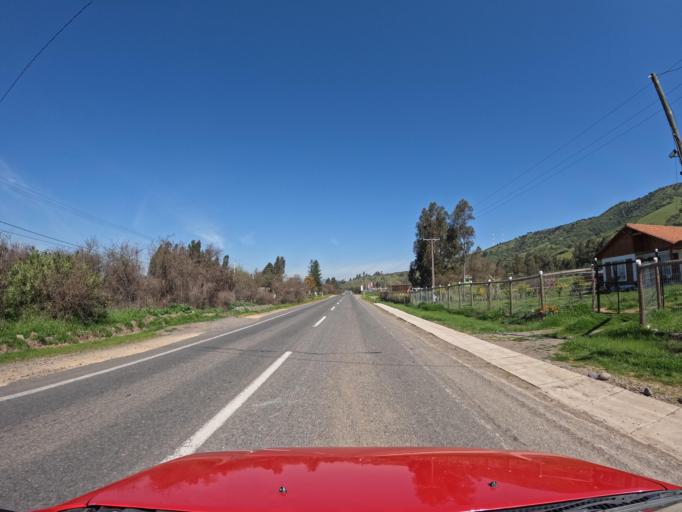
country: CL
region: Maule
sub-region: Provincia de Talca
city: Talca
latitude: -35.0808
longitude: -71.6371
